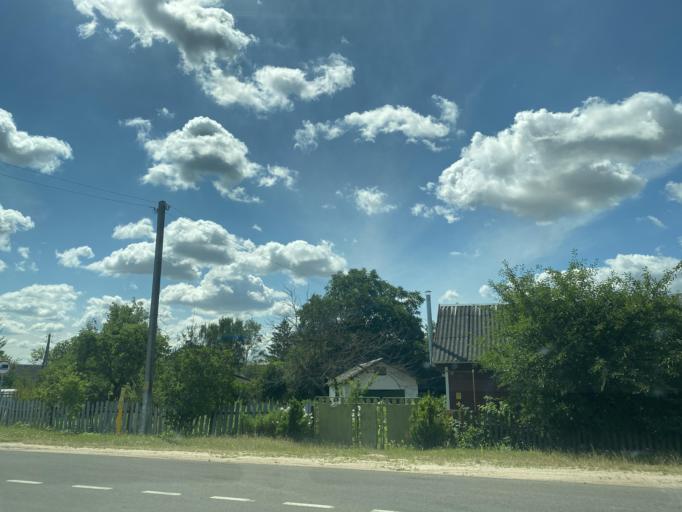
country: BY
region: Brest
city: Ivanava
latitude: 52.1423
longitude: 25.5468
